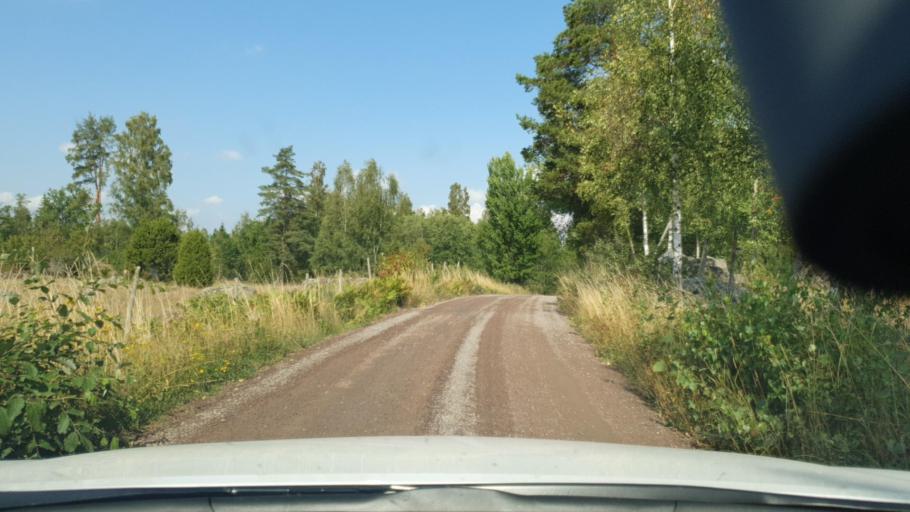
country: SE
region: Kalmar
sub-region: Hultsfreds Kommun
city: Malilla
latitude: 57.3166
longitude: 15.8121
